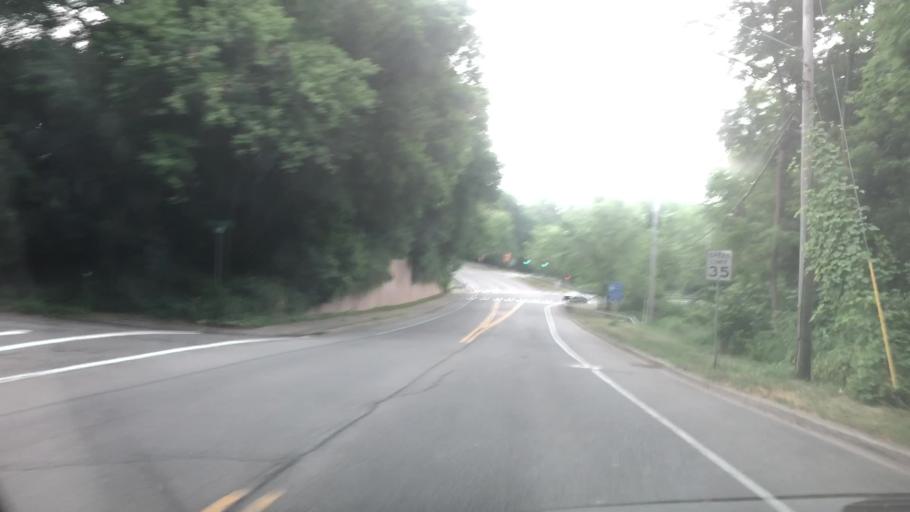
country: US
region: New York
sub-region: Monroe County
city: East Rochester
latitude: 43.1225
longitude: -77.4759
